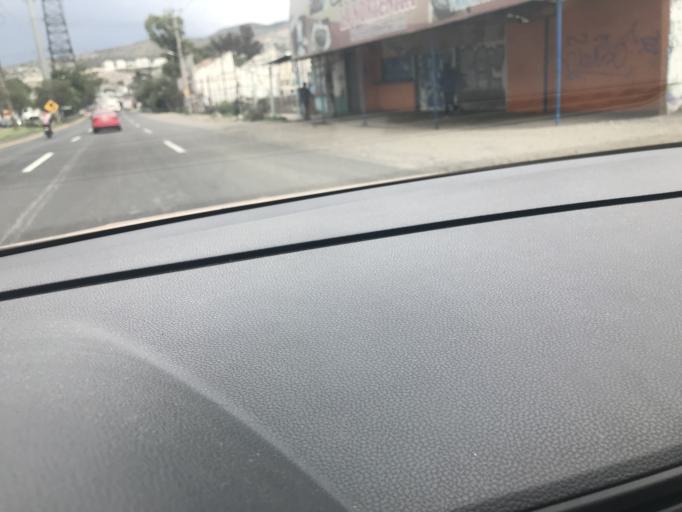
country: MX
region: Mexico
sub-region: La Paz
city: El Pino
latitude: 19.3549
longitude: -98.9612
